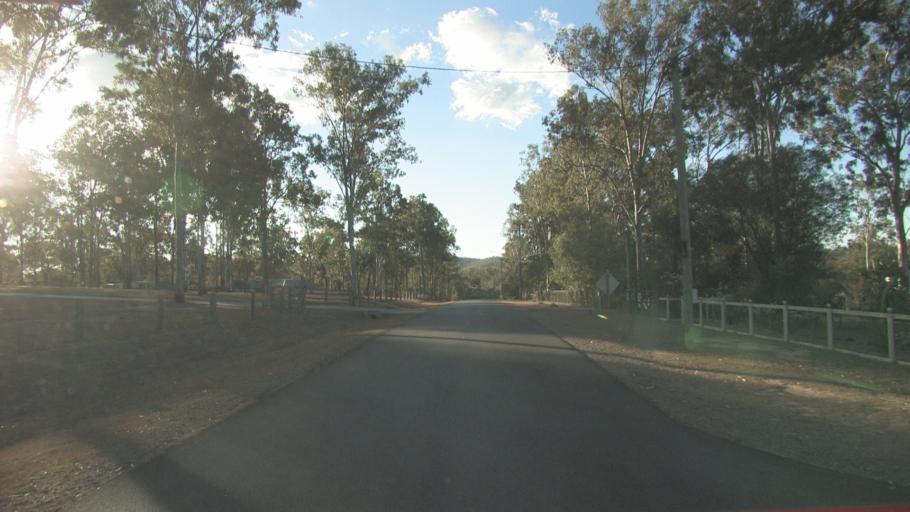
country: AU
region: Queensland
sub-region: Logan
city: Cedar Vale
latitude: -27.8560
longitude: 153.0979
